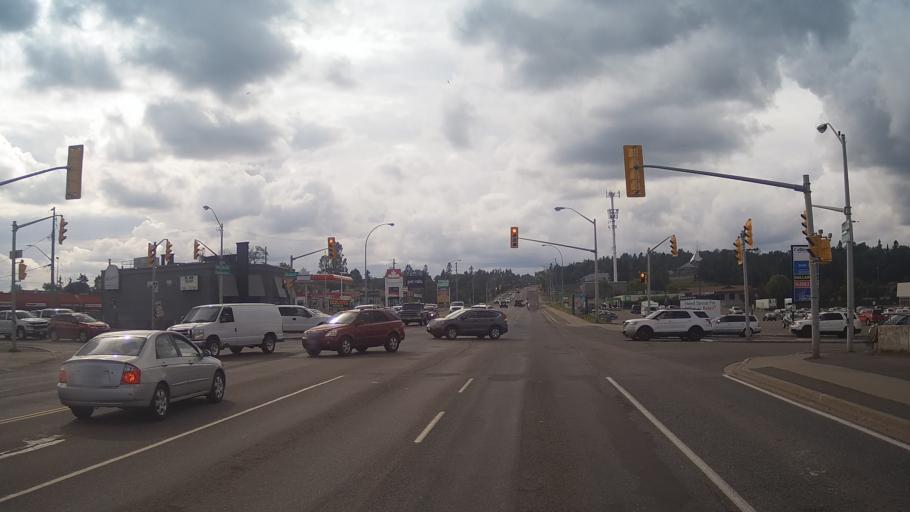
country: CA
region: Ontario
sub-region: Thunder Bay District
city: Thunder Bay
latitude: 48.4514
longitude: -89.2531
